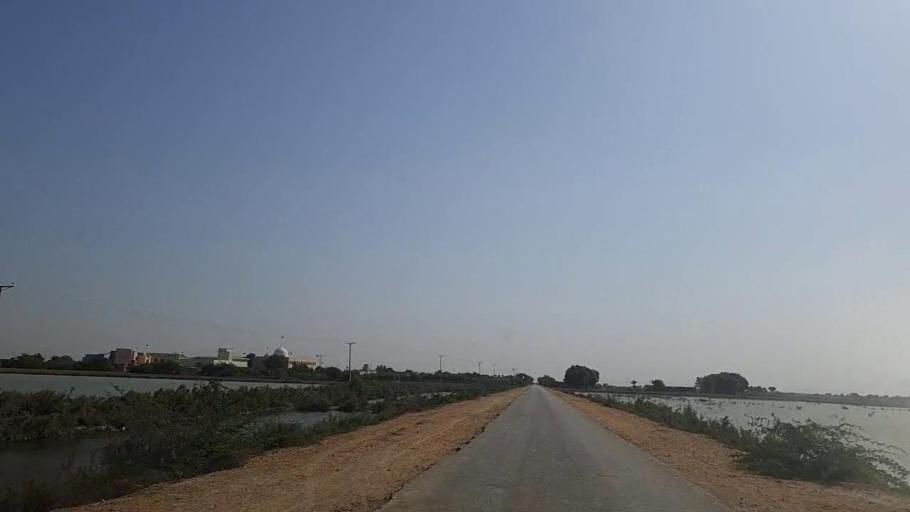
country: PK
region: Sindh
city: Mirpur Batoro
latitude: 24.6435
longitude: 68.2901
